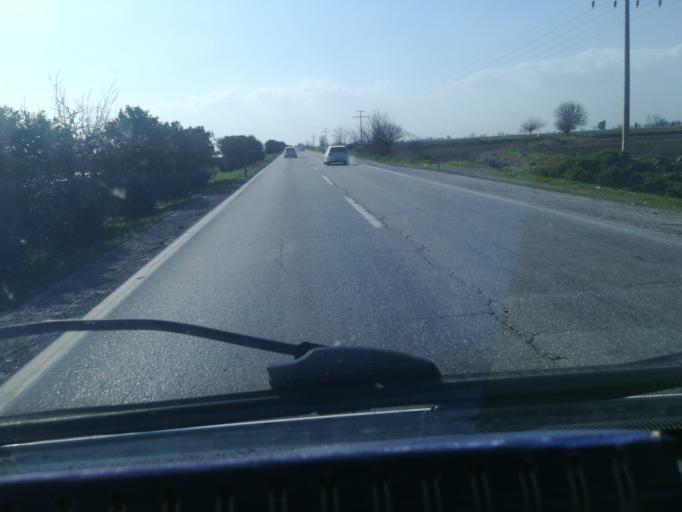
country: TR
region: Osmaniye
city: Toprakkale
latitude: 37.0745
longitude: 36.0582
